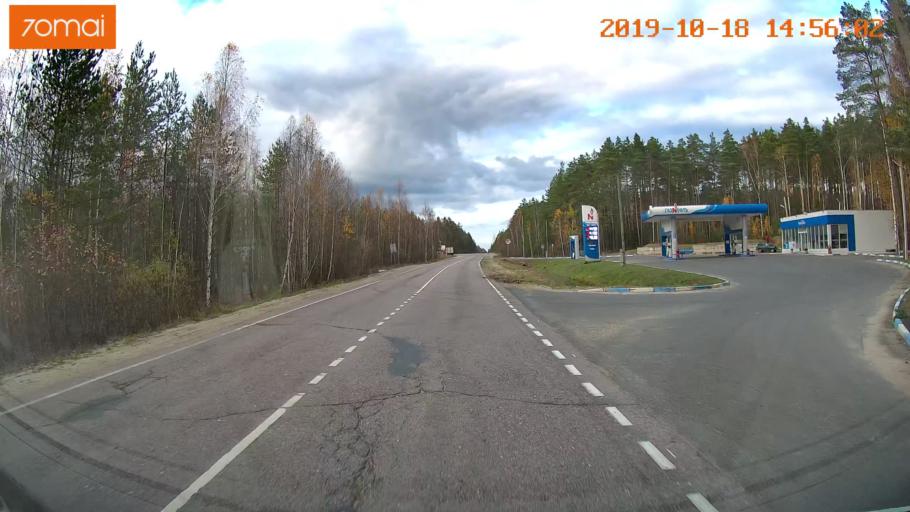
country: RU
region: Vladimir
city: Kurlovo
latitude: 55.4596
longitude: 40.5894
